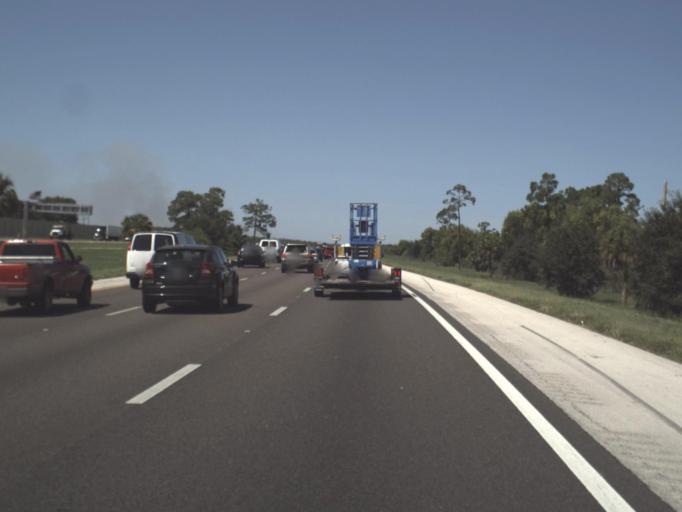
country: US
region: Florida
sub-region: Lee County
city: Bonita Springs
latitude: 26.3540
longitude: -81.7558
